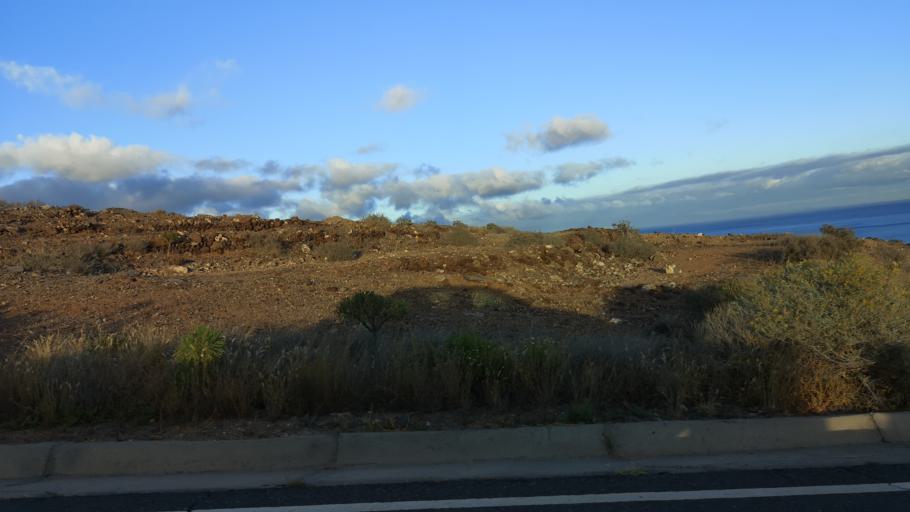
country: ES
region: Canary Islands
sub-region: Provincia de Santa Cruz de Tenerife
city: Alajero
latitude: 28.0279
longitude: -17.2066
